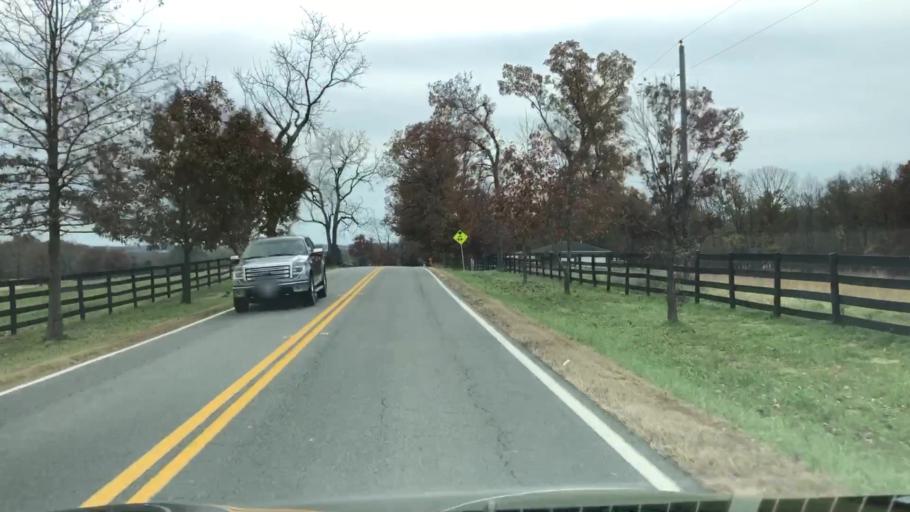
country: US
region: Virginia
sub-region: Fauquier County
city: New Baltimore
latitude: 38.7676
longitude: -77.6809
